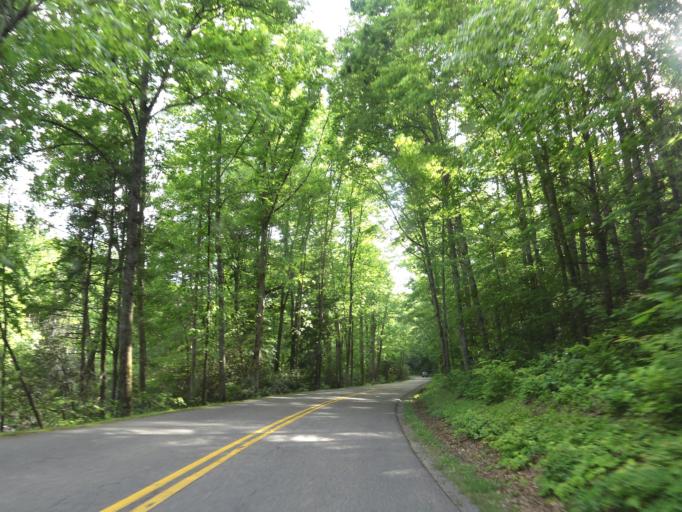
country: US
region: Tennessee
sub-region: Sevier County
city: Gatlinburg
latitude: 35.6657
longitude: -83.6029
